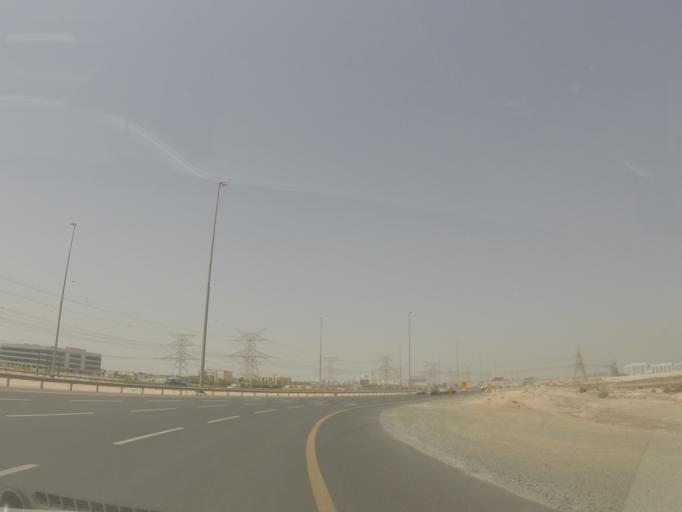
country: AE
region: Dubai
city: Dubai
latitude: 25.0055
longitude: 55.1731
